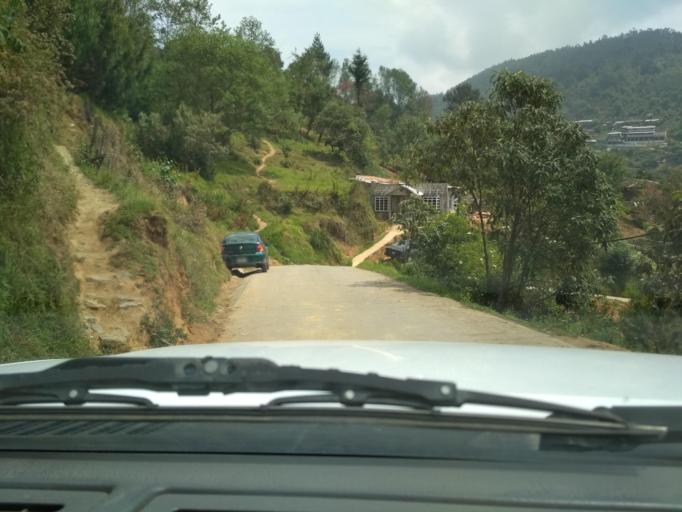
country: MX
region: Veracruz
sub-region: Camerino Z. Mendoza
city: Necoxtla
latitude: 18.7799
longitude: -97.1545
